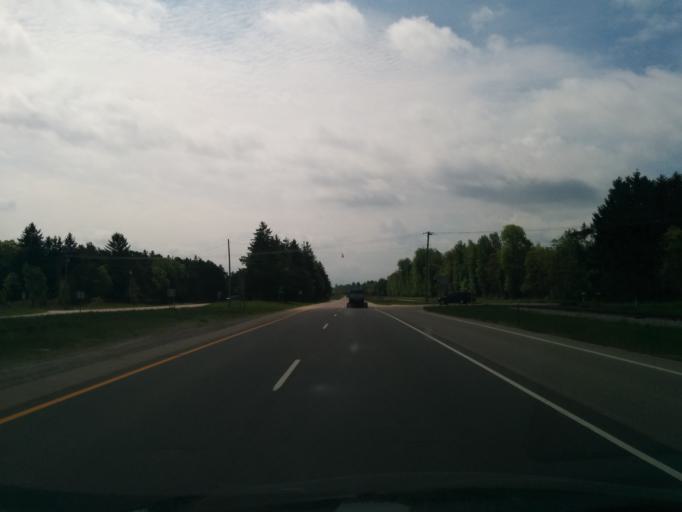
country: US
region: Michigan
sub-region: Ottawa County
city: Grand Haven
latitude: 42.9876
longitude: -86.1932
